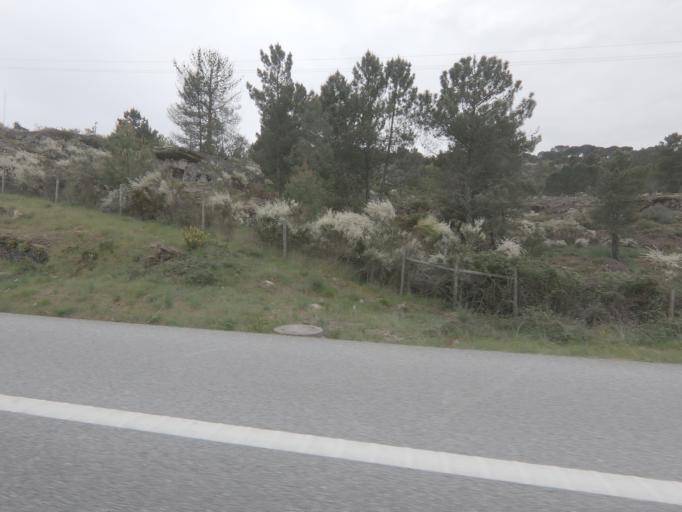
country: PT
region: Viseu
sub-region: Mangualde
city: Mangualde
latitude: 40.6169
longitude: -7.7419
